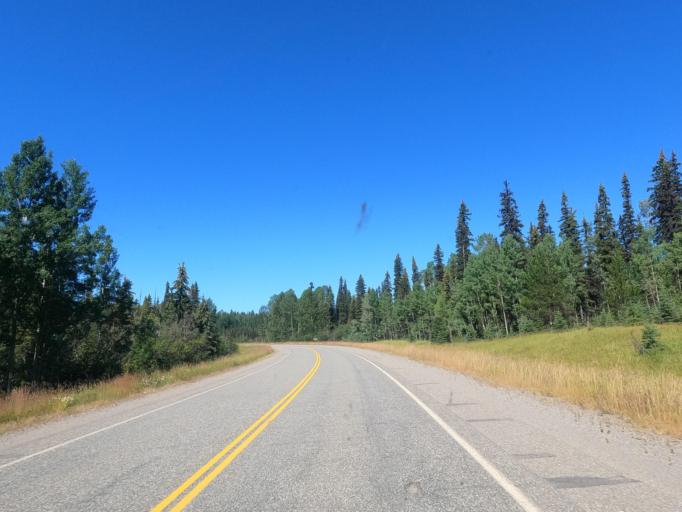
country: CA
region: British Columbia
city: Quesnel
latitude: 53.0554
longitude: -122.1680
